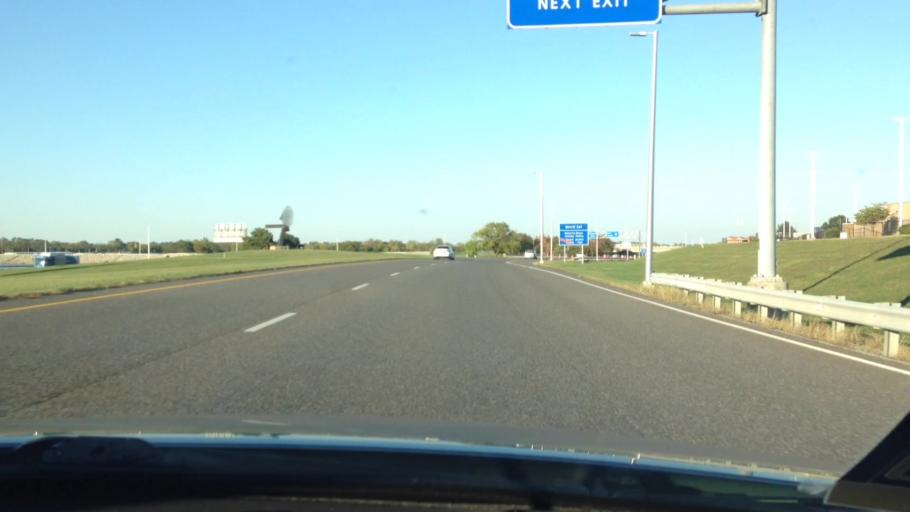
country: US
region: Missouri
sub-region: Platte County
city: Weatherby Lake
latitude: 39.3054
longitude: -94.7110
